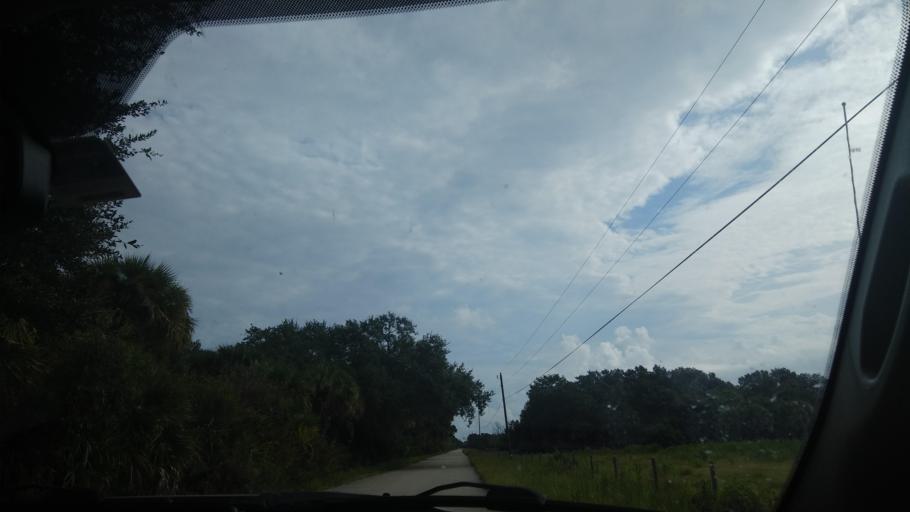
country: US
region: Florida
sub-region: Indian River County
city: Fellsmere
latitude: 27.7004
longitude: -80.7854
